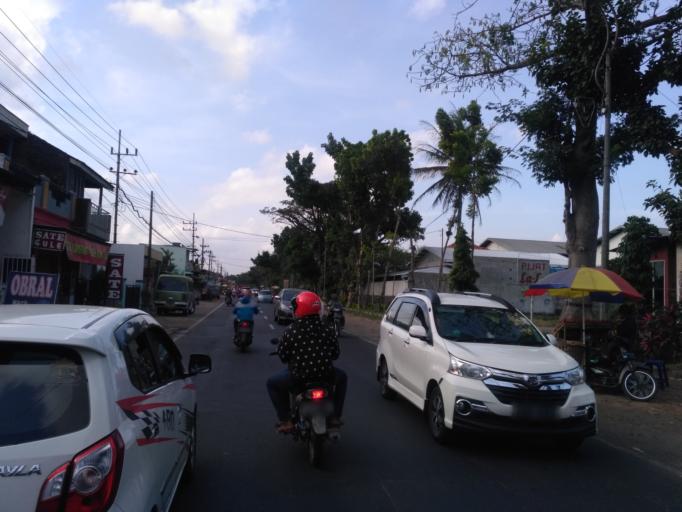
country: ID
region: East Java
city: Golek
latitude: -8.0542
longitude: 112.6044
